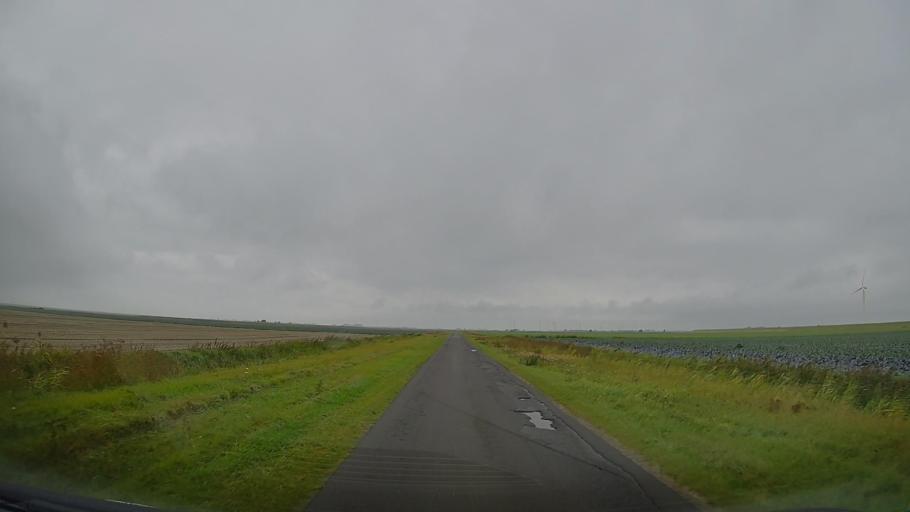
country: DE
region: Schleswig-Holstein
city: Friedrichsgabekoog
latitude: 54.1079
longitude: 8.9857
